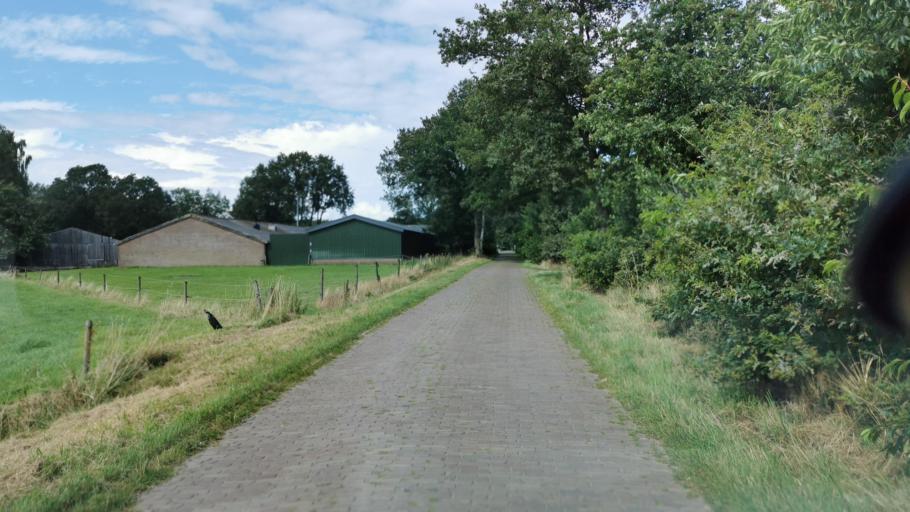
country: NL
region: Overijssel
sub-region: Gemeente Losser
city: Losser
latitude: 52.2536
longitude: 6.9551
